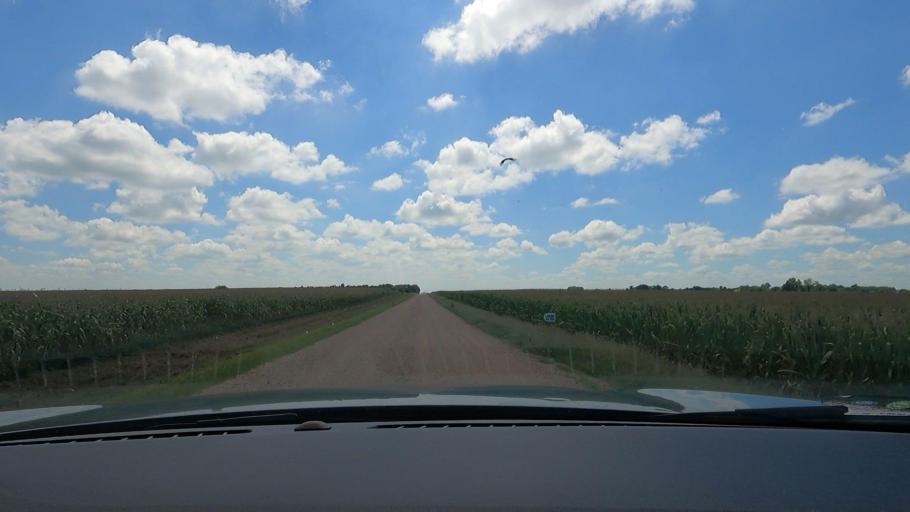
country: US
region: Nebraska
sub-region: Saunders County
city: Wahoo
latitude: 41.2727
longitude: -96.5418
